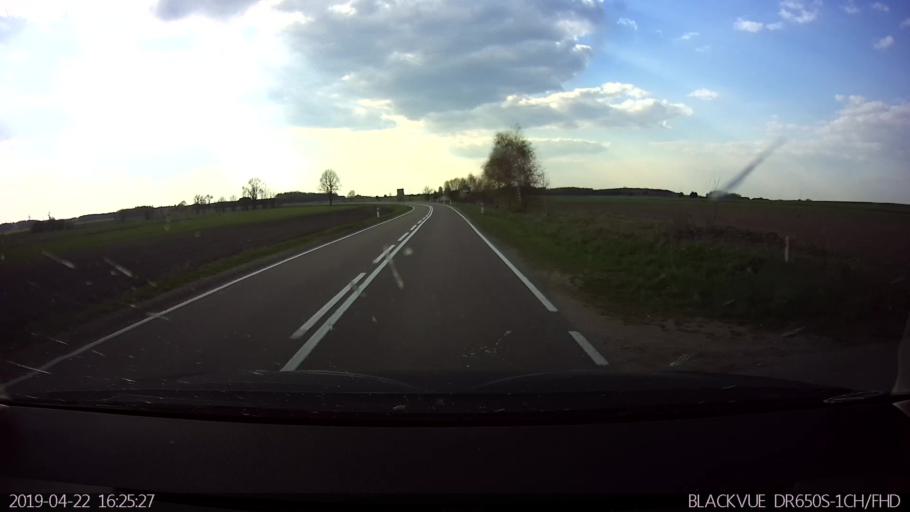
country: PL
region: Podlasie
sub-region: Powiat hajnowski
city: Kleszczele
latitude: 52.5555
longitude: 23.2443
